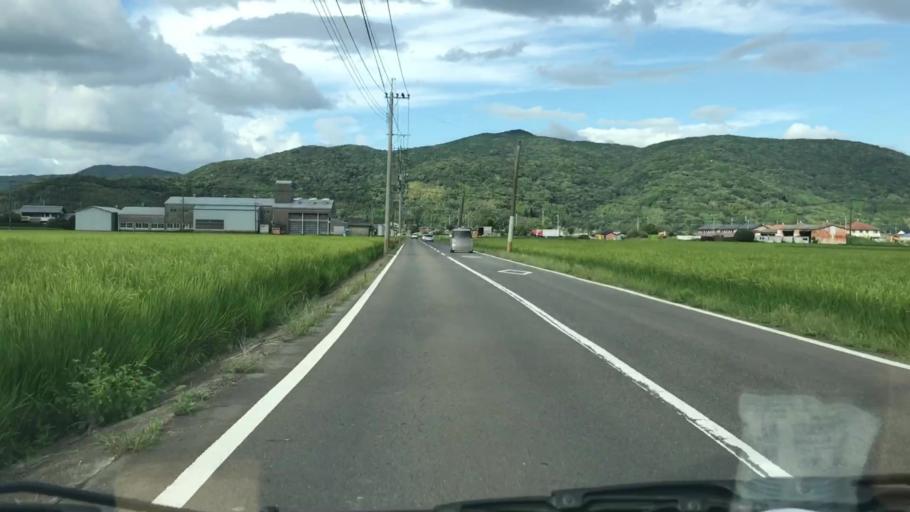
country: JP
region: Saga Prefecture
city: Kashima
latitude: 33.1210
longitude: 130.0715
